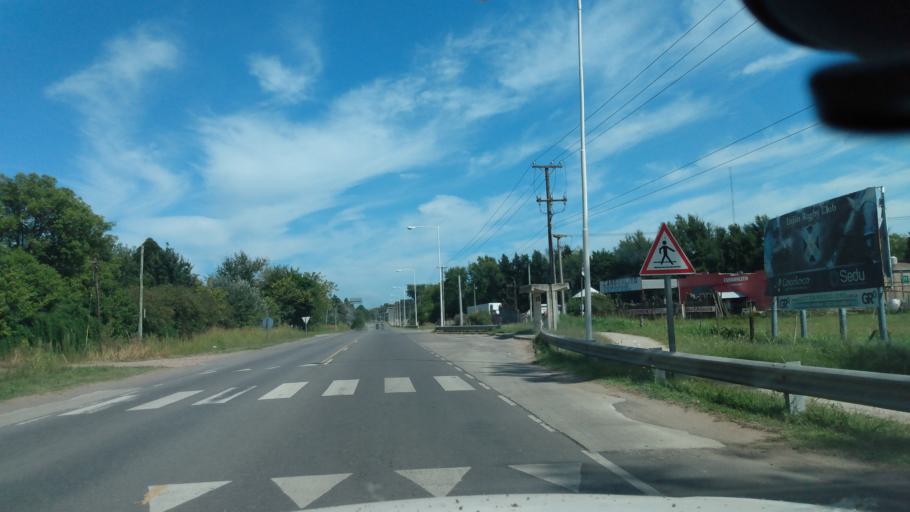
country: AR
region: Buenos Aires
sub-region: Partido de Lujan
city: Lujan
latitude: -34.5501
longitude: -59.1318
